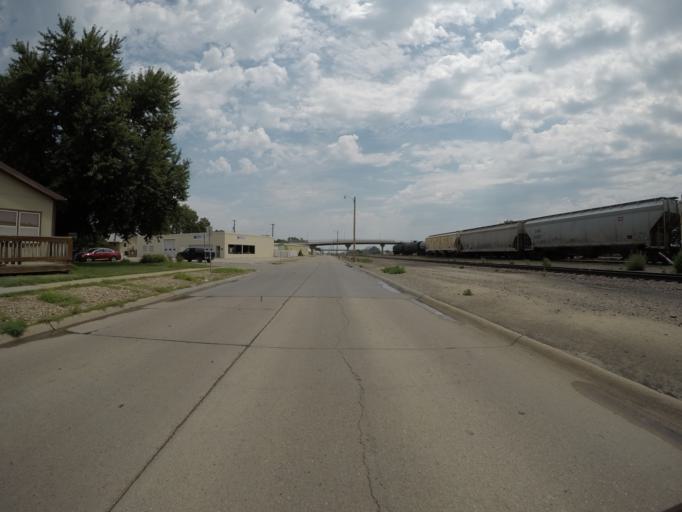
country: US
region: Nebraska
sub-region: Buffalo County
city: Kearney
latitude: 40.6967
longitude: -99.0752
